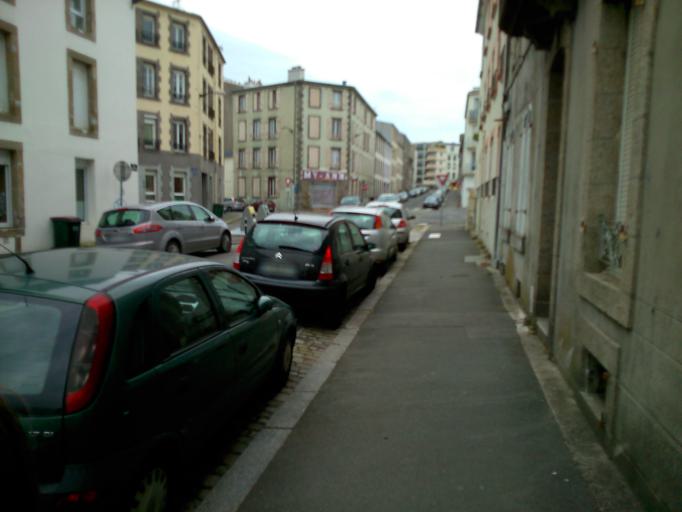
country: FR
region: Brittany
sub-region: Departement du Finistere
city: Brest
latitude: 48.3956
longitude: -4.4733
